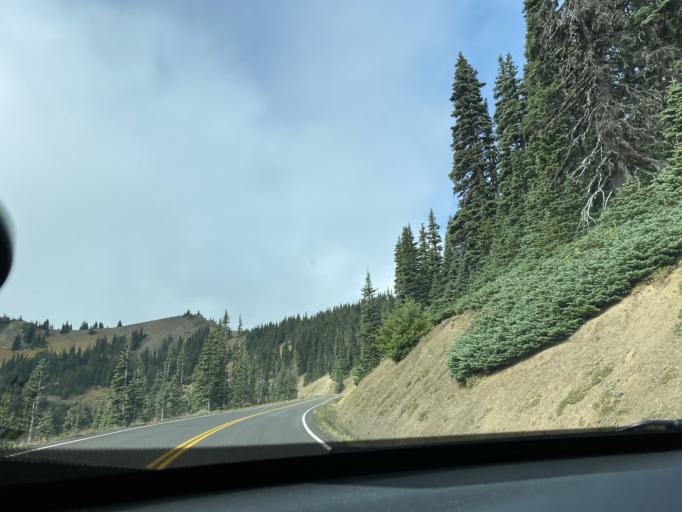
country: US
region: Washington
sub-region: Clallam County
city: Port Angeles
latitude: 47.9730
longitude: -123.4803
